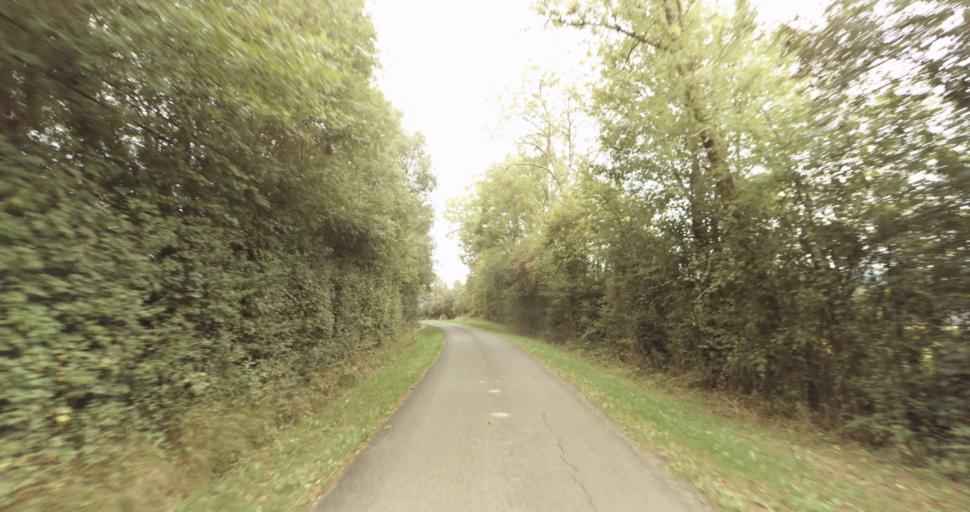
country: FR
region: Lower Normandy
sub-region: Departement de l'Orne
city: Gace
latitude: 48.7303
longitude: 0.3154
